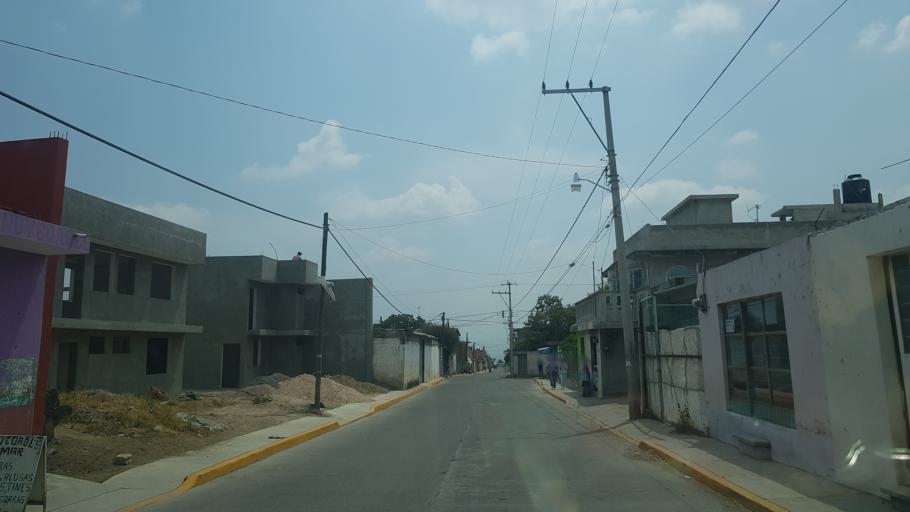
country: MX
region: Puebla
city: Domingo Arenas
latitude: 19.1394
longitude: -98.4564
